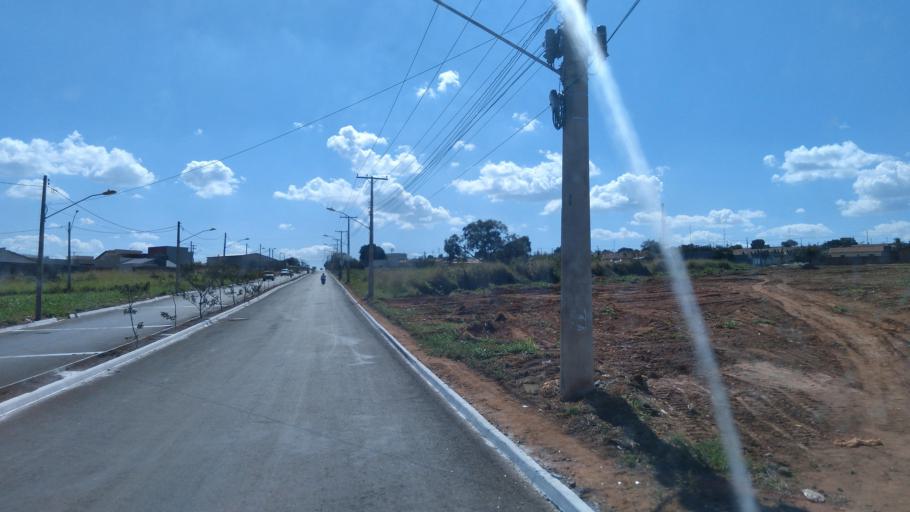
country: BR
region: Goias
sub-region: Mineiros
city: Mineiros
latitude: -17.5528
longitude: -52.5407
